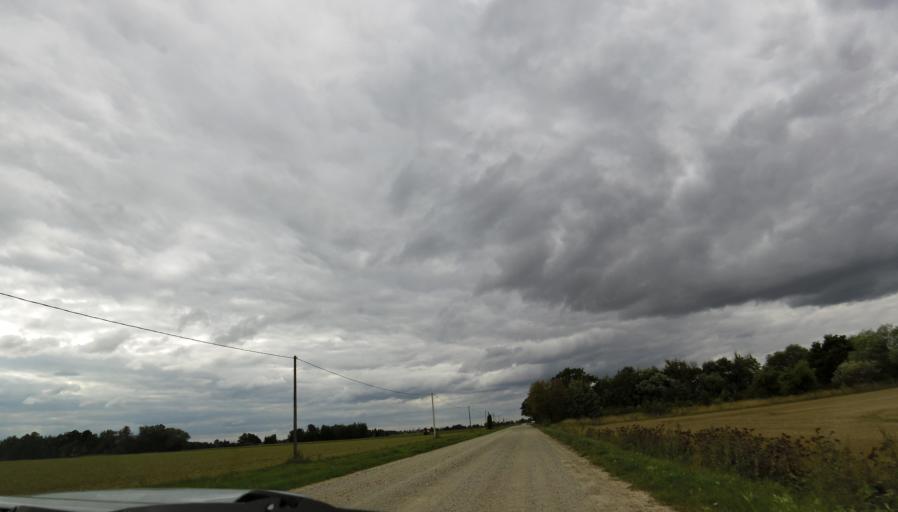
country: LT
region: Panevezys
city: Pasvalys
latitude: 56.0596
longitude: 24.2461
